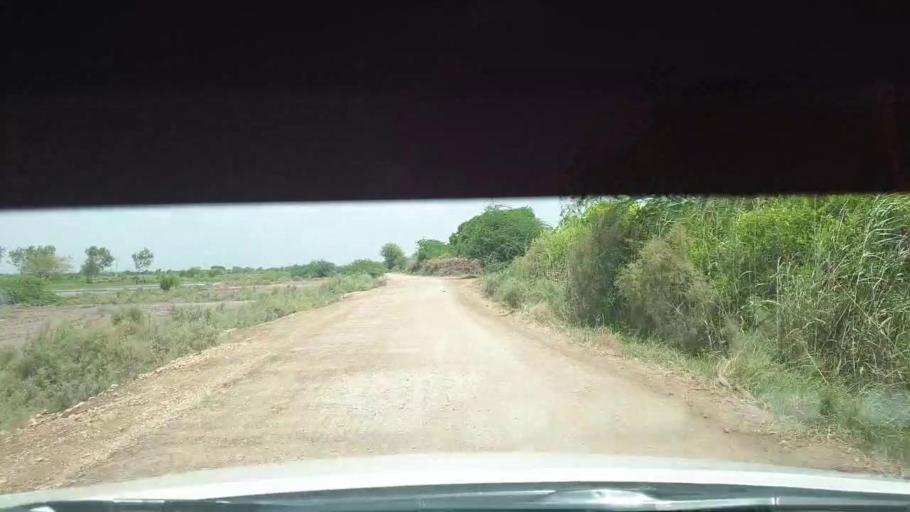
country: PK
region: Sindh
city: Kadhan
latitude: 24.5092
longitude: 68.9773
